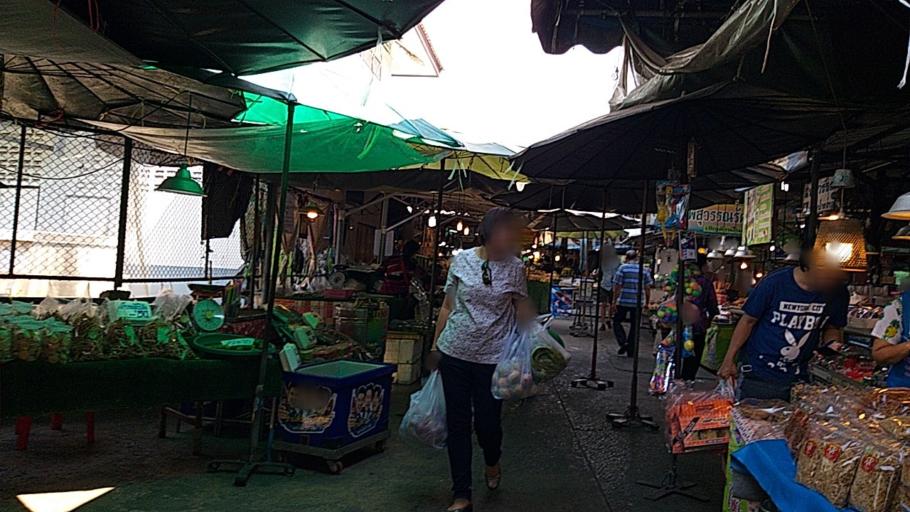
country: TH
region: Nakhon Pathom
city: Salaya
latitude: 13.7705
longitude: 100.2841
